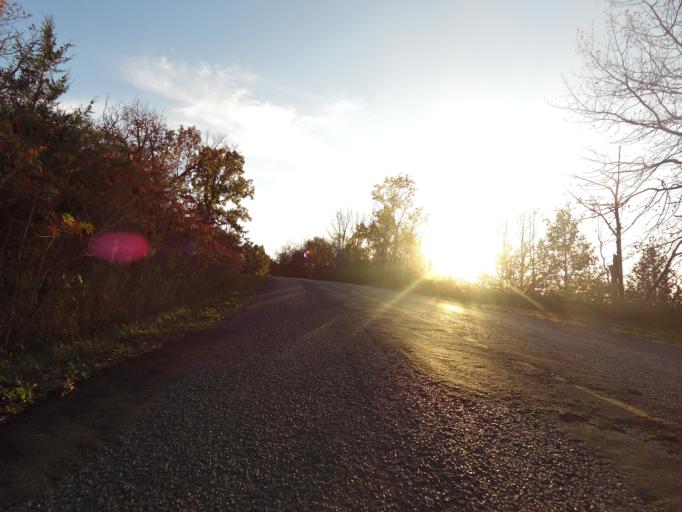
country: CA
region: Ontario
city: Gananoque
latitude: 44.3892
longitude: -76.3270
